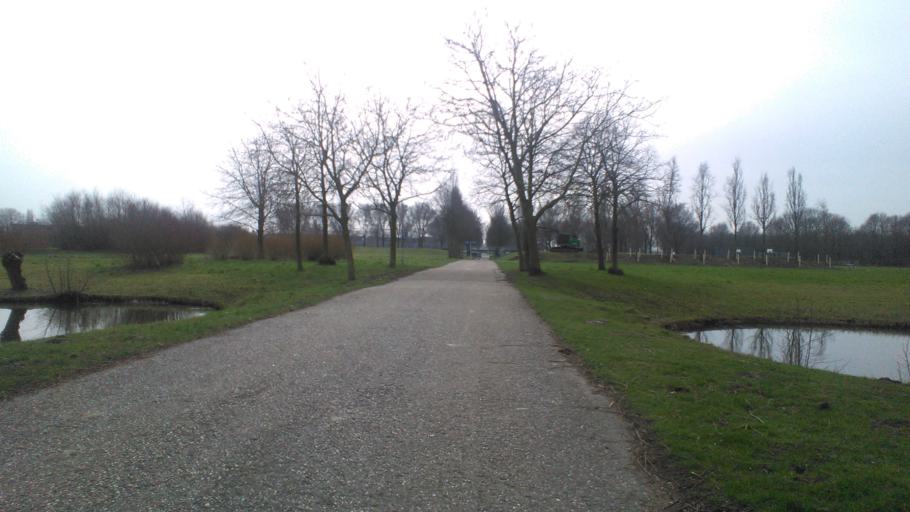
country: NL
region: South Holland
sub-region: Gemeente Zoetermeer
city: Zoetermeer
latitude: 52.0439
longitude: 4.4590
